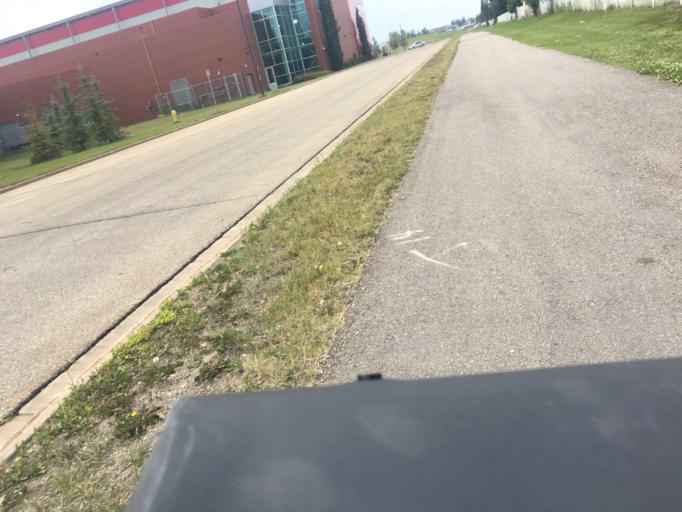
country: CA
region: Alberta
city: Grande Prairie
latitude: 55.1449
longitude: -118.8111
